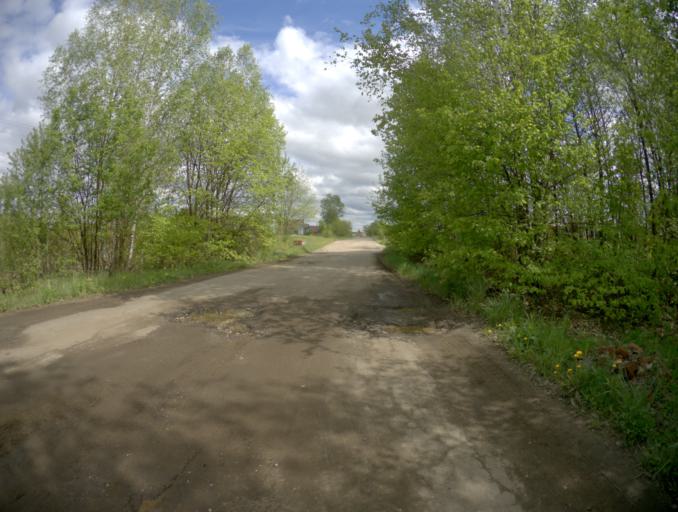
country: RU
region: Vladimir
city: Velikodvorskiy
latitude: 55.1199
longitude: 40.8877
